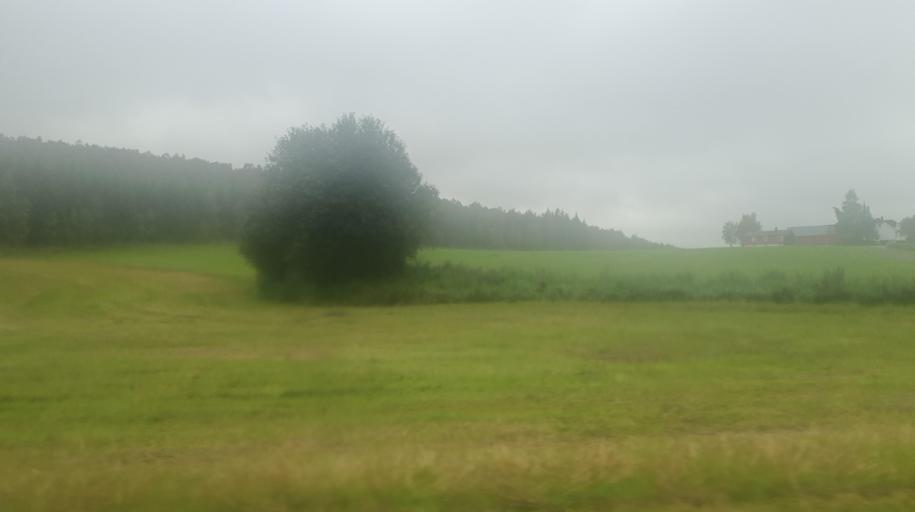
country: NO
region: Nord-Trondelag
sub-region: Levanger
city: Skogn
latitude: 63.6190
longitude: 11.1650
